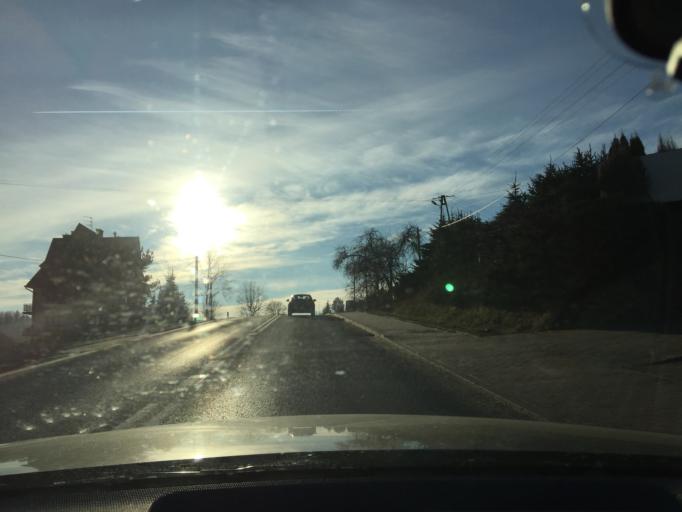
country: PL
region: Lesser Poland Voivodeship
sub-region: Powiat wadowicki
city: Izdebnik
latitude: 49.8672
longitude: 19.7614
